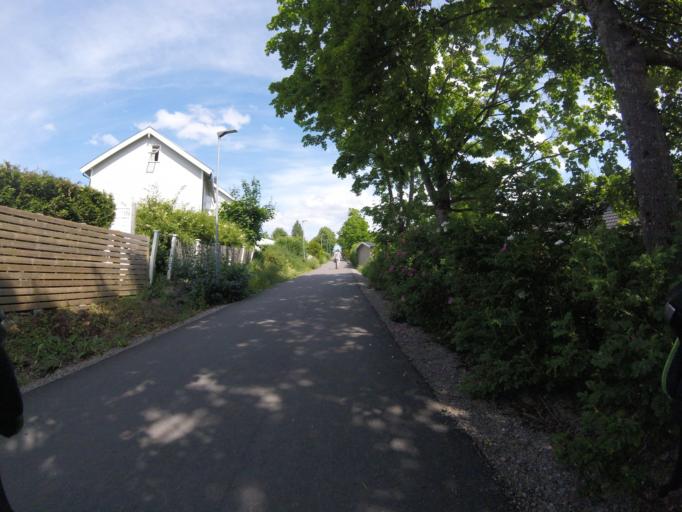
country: NO
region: Akershus
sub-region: Skedsmo
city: Lillestrom
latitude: 59.9903
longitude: 11.0360
